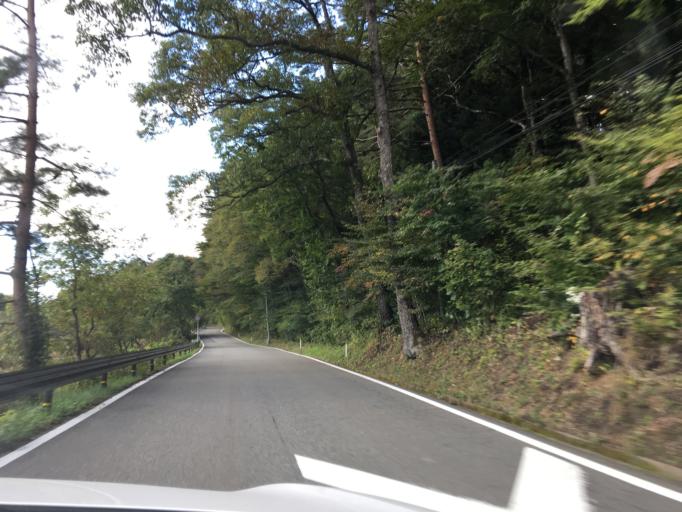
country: JP
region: Fukushima
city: Namie
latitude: 37.5615
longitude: 140.8155
